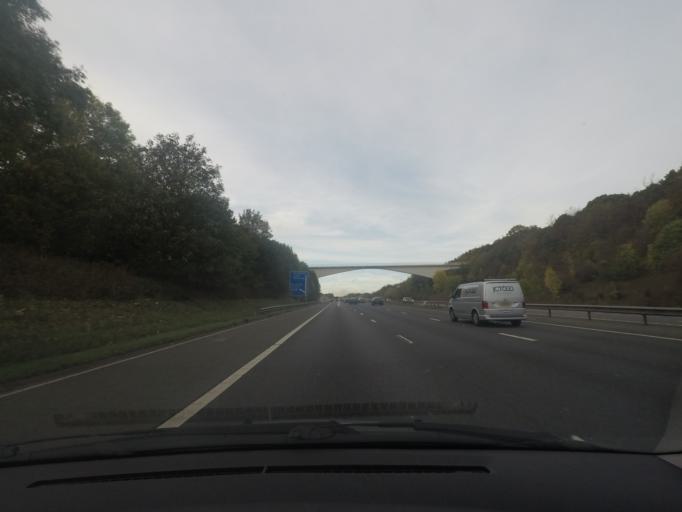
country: GB
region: England
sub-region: Barnsley
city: Stainborough
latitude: 53.5393
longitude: -1.5081
